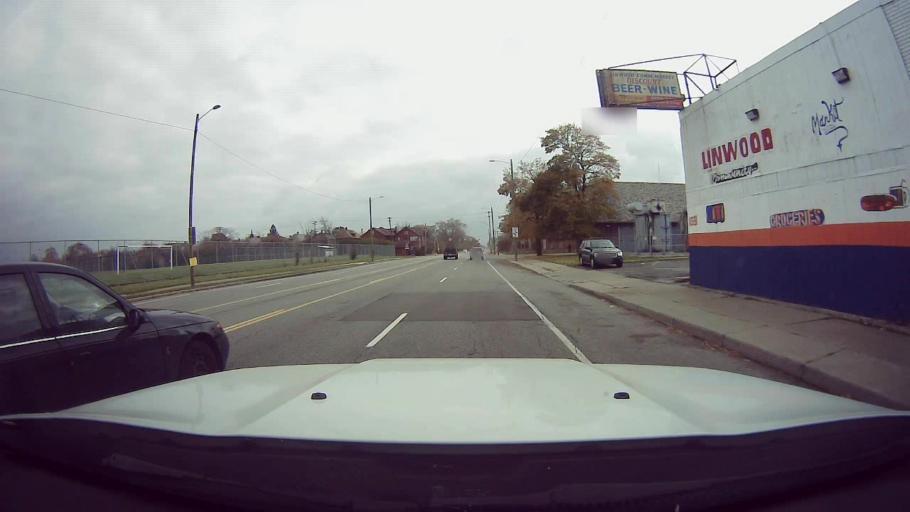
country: US
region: Michigan
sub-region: Wayne County
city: Highland Park
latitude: 42.3811
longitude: -83.1138
